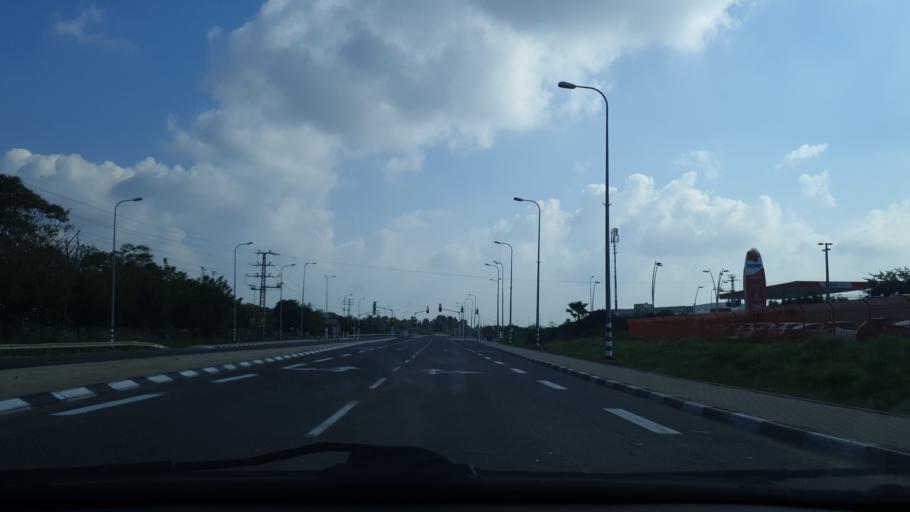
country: IL
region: Central District
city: Kefar Habad
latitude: 31.9609
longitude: 34.8506
